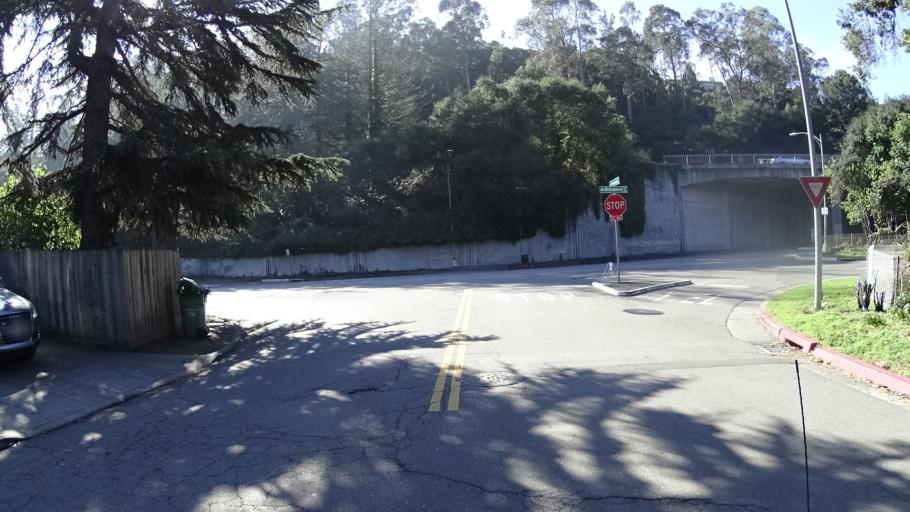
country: US
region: California
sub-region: Alameda County
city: Piedmont
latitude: 37.8416
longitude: -122.2238
